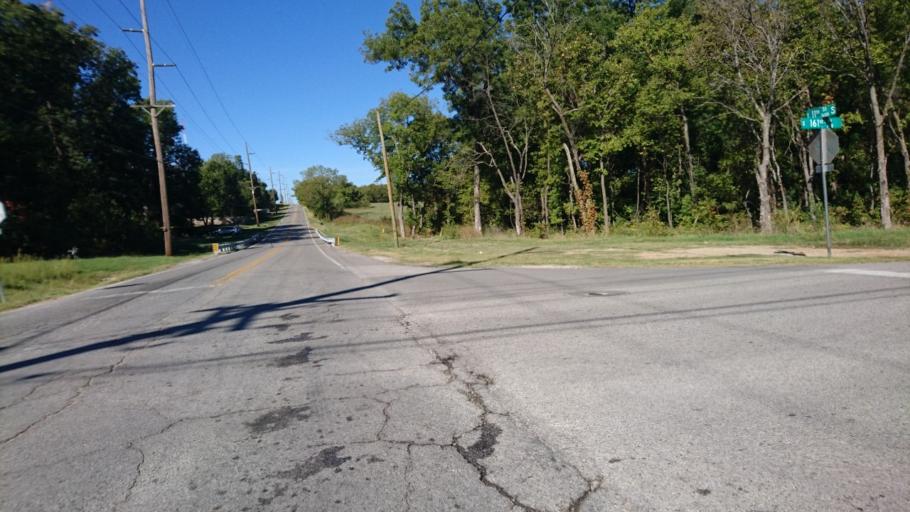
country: US
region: Oklahoma
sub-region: Rogers County
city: Catoosa
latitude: 36.1479
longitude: -95.7975
